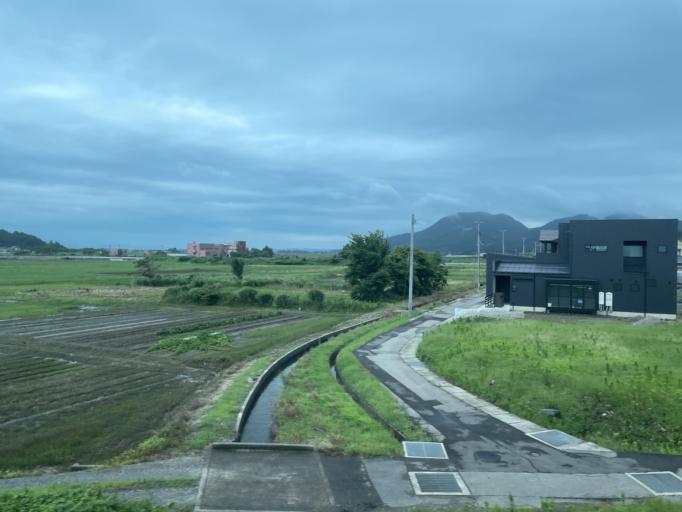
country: JP
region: Niigata
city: Yoshida-kasugacho
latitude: 37.6996
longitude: 138.8375
